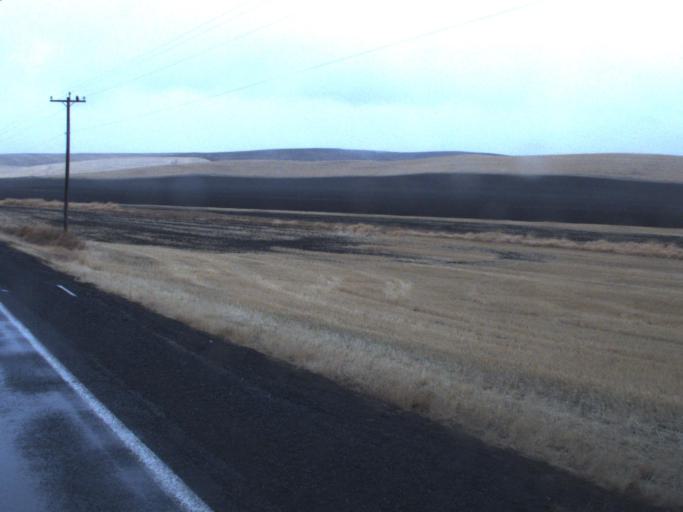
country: US
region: Washington
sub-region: Whitman County
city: Colfax
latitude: 47.0077
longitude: -117.4570
